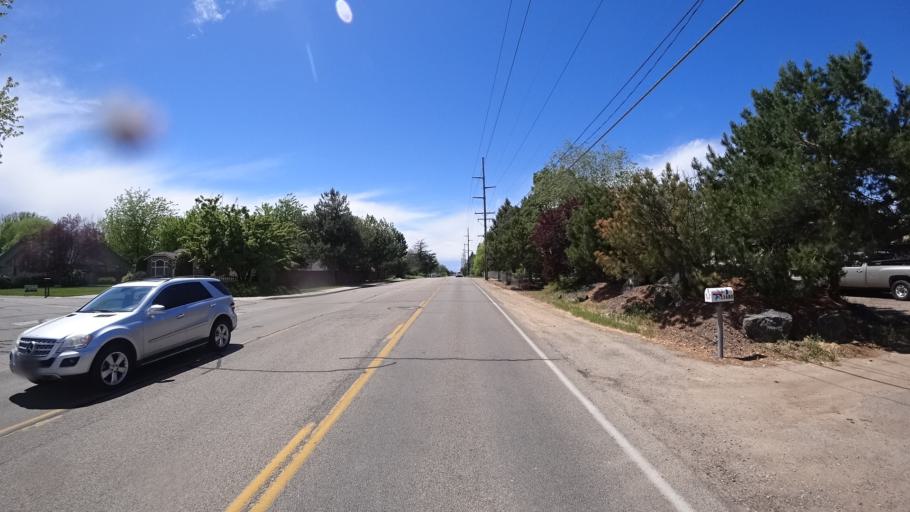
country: US
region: Idaho
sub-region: Ada County
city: Meridian
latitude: 43.5758
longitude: -116.3273
